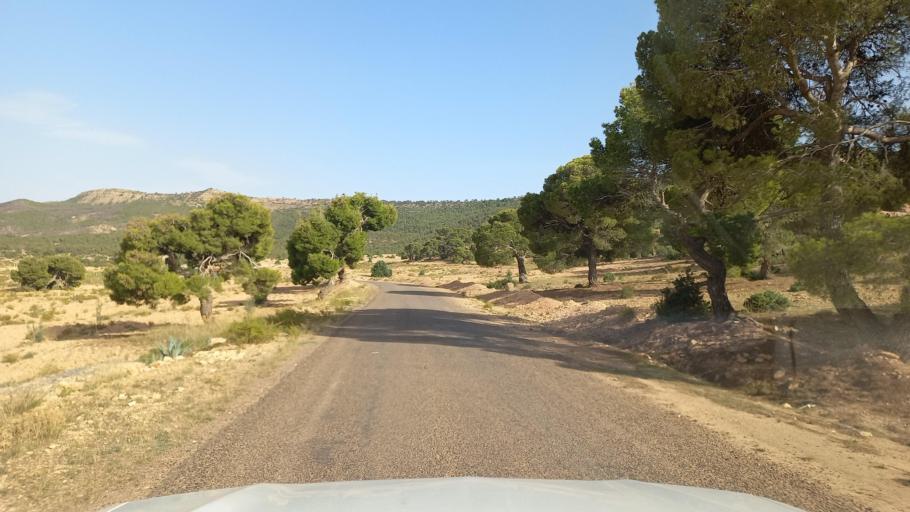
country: TN
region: Al Qasrayn
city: Kasserine
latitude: 35.3332
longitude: 8.8425
